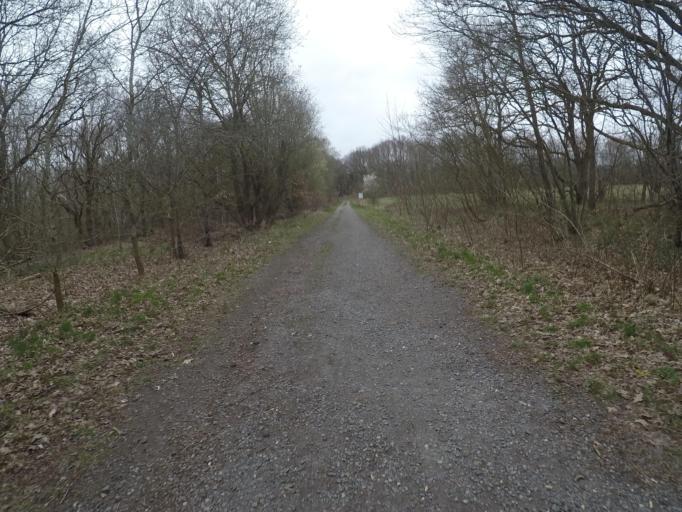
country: DE
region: Lower Saxony
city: Cuxhaven
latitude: 53.8384
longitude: 8.6444
